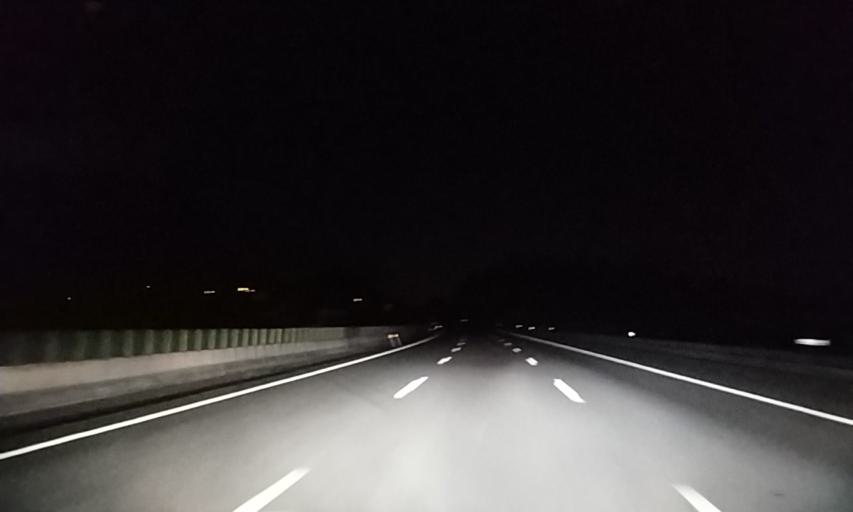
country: PT
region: Aveiro
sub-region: Ovar
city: Valega
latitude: 40.8402
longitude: -8.5550
